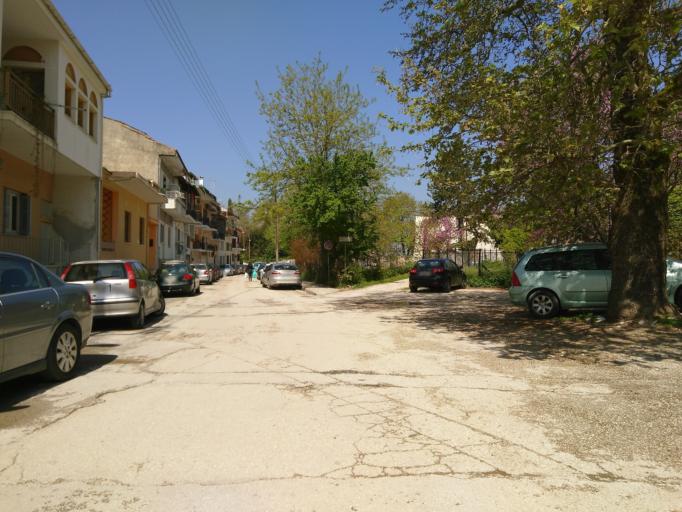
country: GR
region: Epirus
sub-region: Nomos Ioanninon
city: Ioannina
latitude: 39.6722
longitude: 20.8599
